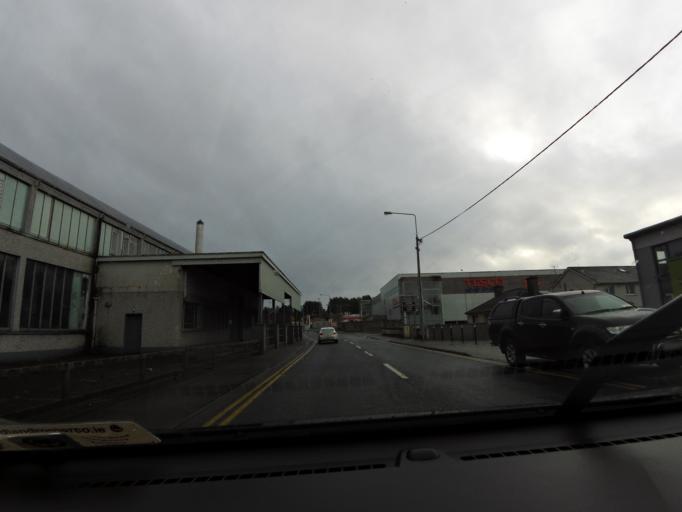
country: IE
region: Munster
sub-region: North Tipperary
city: Roscrea
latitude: 52.9574
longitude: -7.7969
